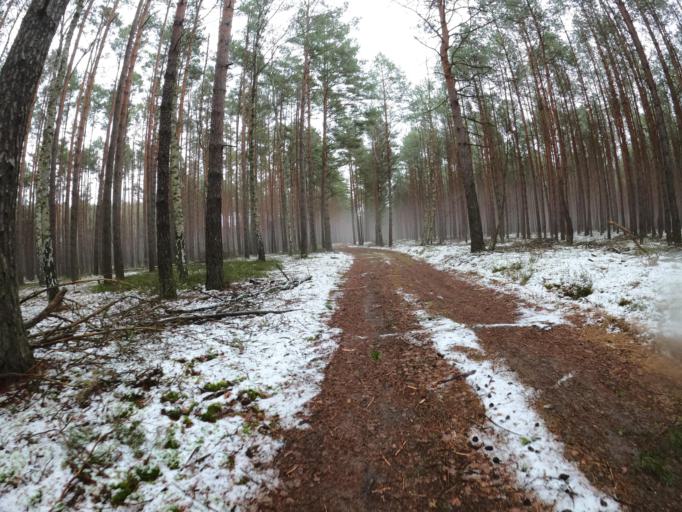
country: PL
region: Lubusz
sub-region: Powiat sulecinski
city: Torzym
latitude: 52.2114
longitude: 14.9683
